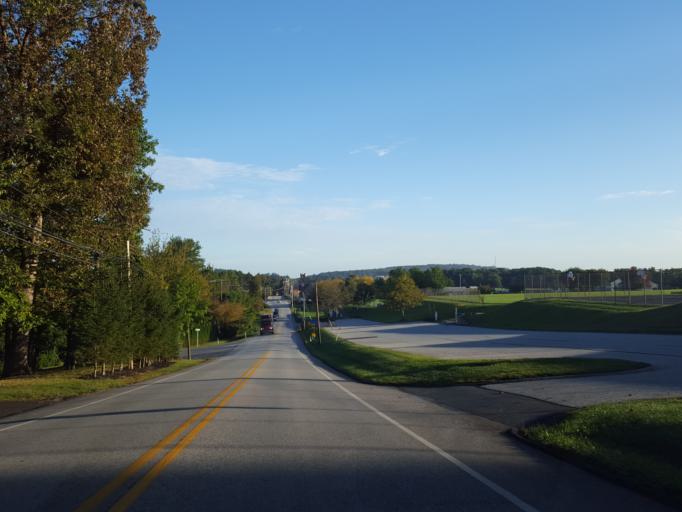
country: US
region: Pennsylvania
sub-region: York County
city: Red Lion
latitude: 39.9240
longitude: -76.6071
